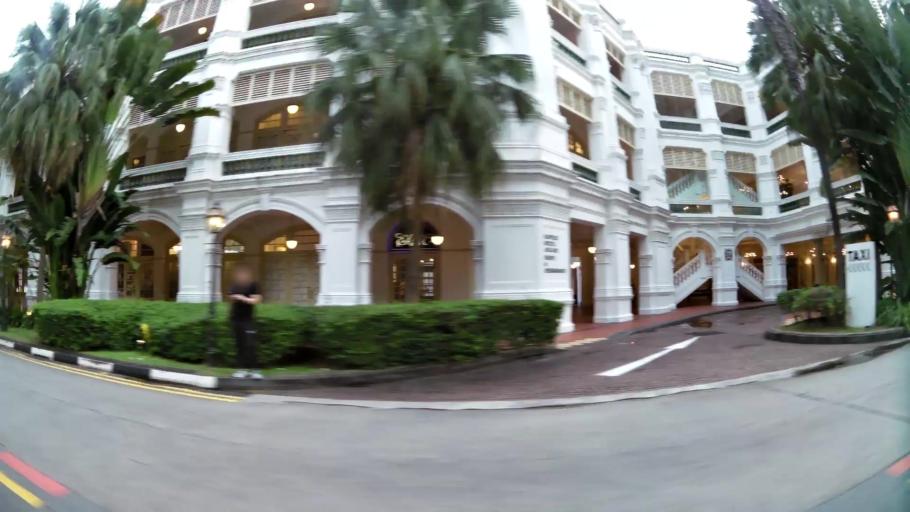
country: SG
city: Singapore
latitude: 1.2960
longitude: 103.8539
